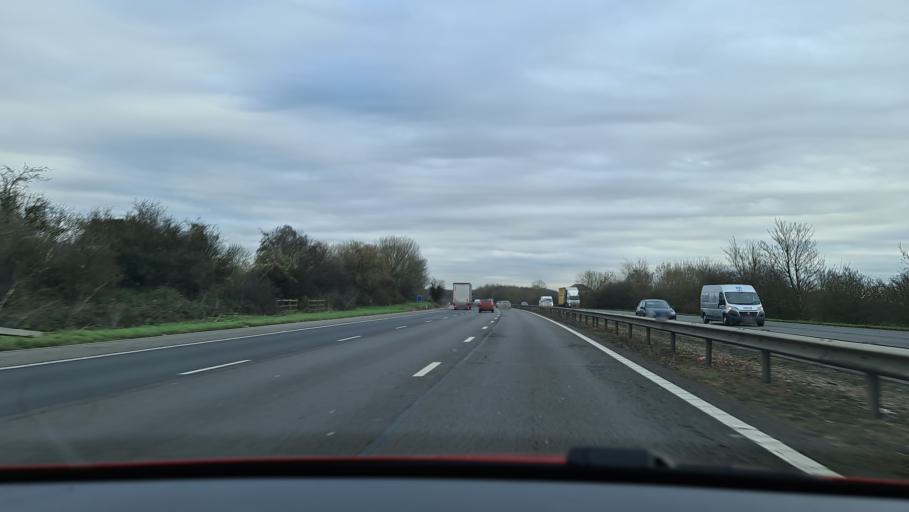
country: GB
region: England
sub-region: Buckinghamshire
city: High Wycombe
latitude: 51.6105
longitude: -0.7304
